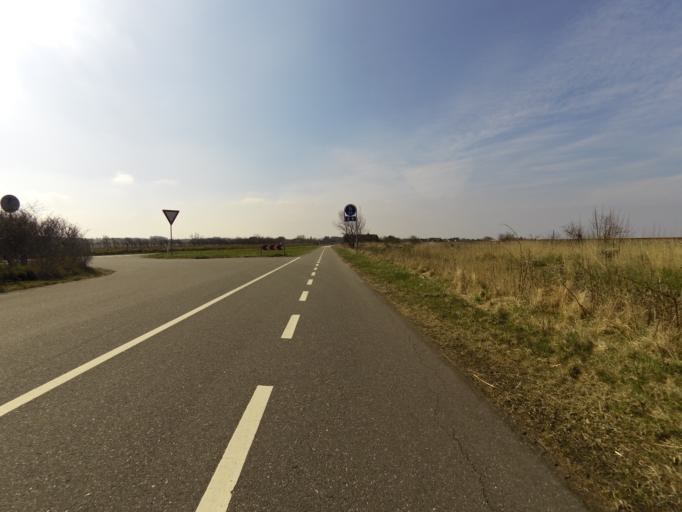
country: DK
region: Central Jutland
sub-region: Holstebro Kommune
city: Vinderup
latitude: 56.4736
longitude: 8.7310
